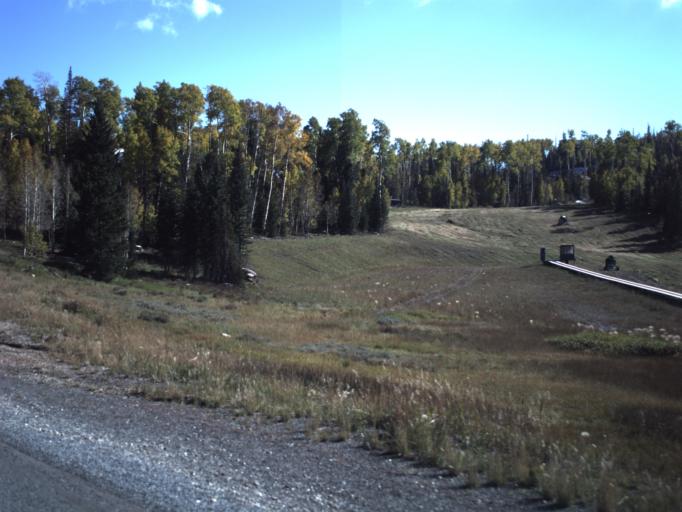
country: US
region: Utah
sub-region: Iron County
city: Parowan
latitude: 37.7029
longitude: -112.8484
